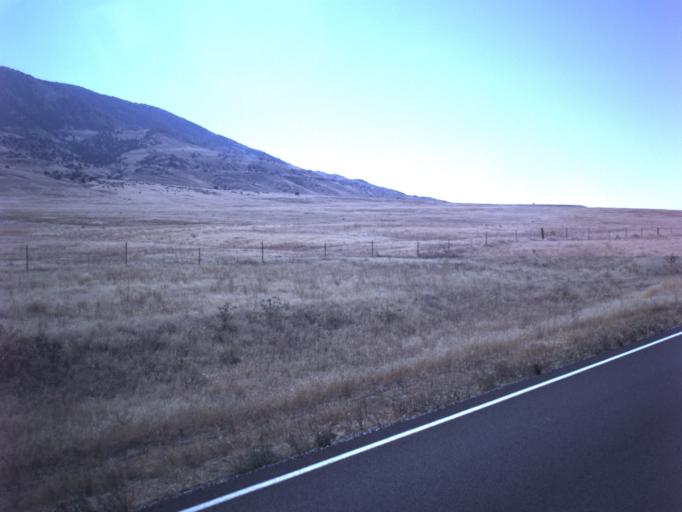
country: US
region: Utah
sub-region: Tooele County
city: Grantsville
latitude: 40.5683
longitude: -112.7317
